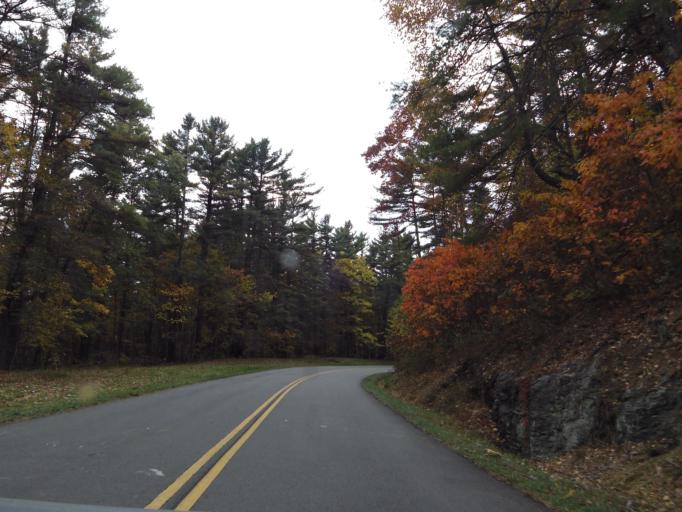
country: US
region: North Carolina
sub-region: Ashe County
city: Jefferson
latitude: 36.3726
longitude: -81.3325
